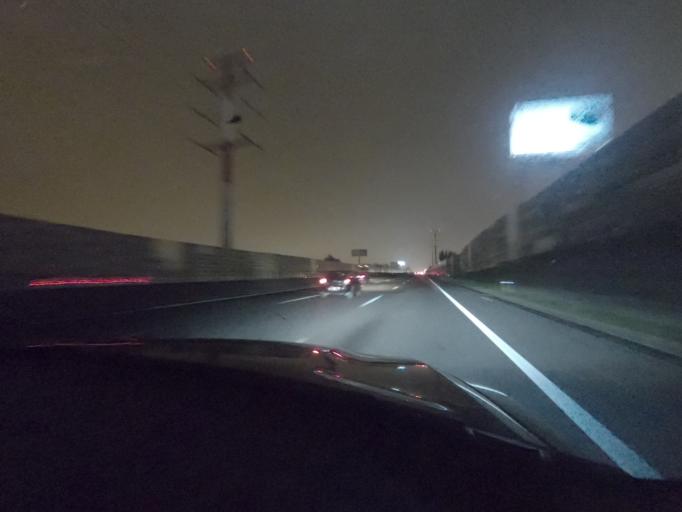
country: PT
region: Lisbon
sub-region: Loures
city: Sao Joao da Talha
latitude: 38.8321
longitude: -9.0970
